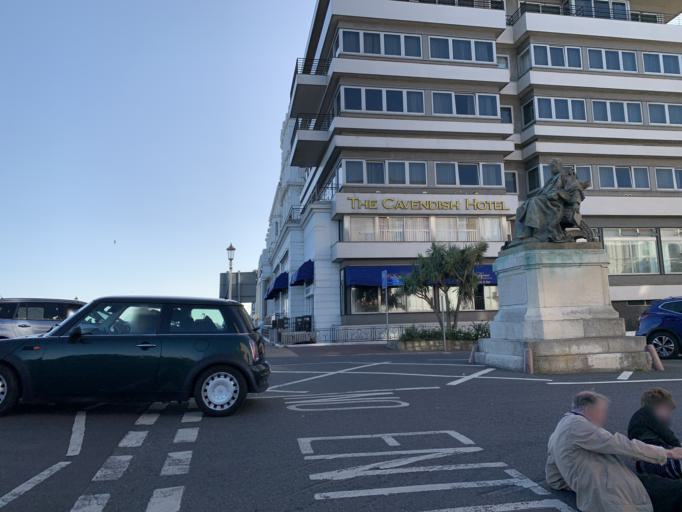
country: GB
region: England
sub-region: East Sussex
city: Eastbourne
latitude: 50.7647
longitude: 0.2891
